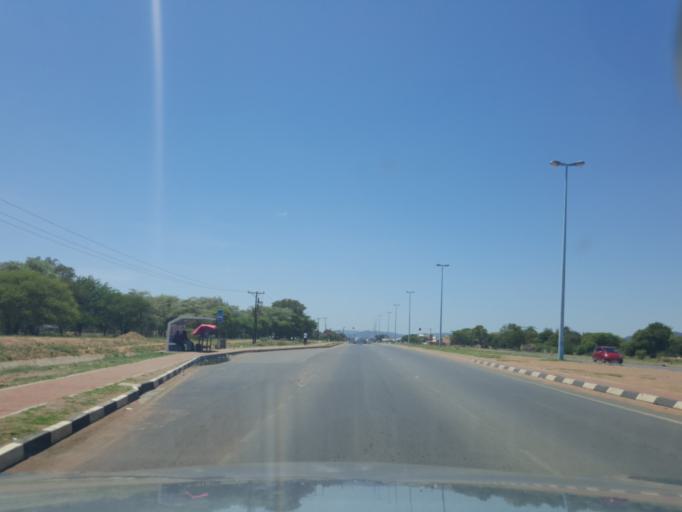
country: BW
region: Kweneng
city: Mogoditshane
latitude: -24.6073
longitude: 25.8581
